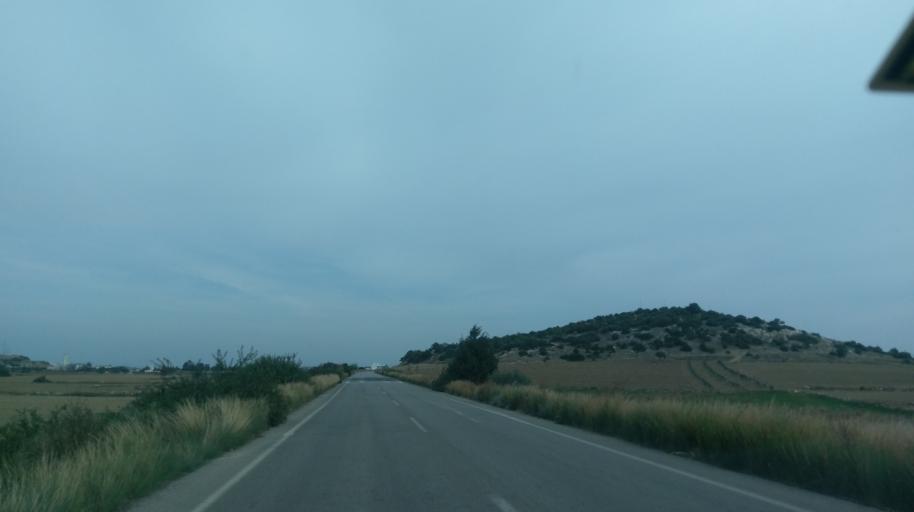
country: CY
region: Ammochostos
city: Leonarisso
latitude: 35.3979
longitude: 34.0690
